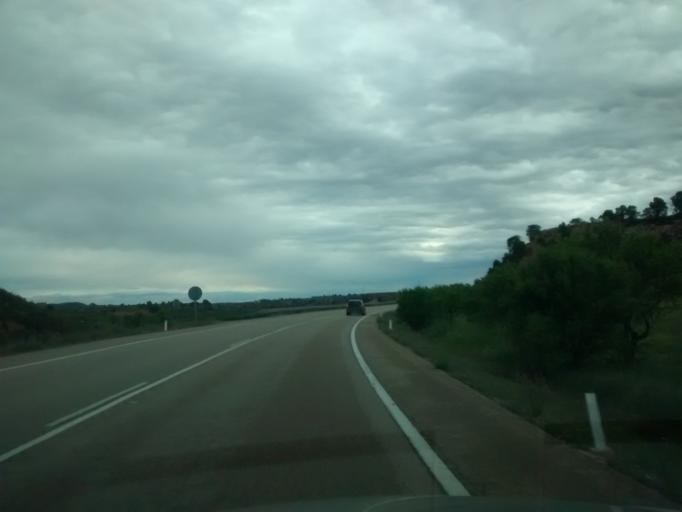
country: ES
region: Aragon
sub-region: Provincia de Zaragoza
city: Maella
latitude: 41.1791
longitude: 0.0521
